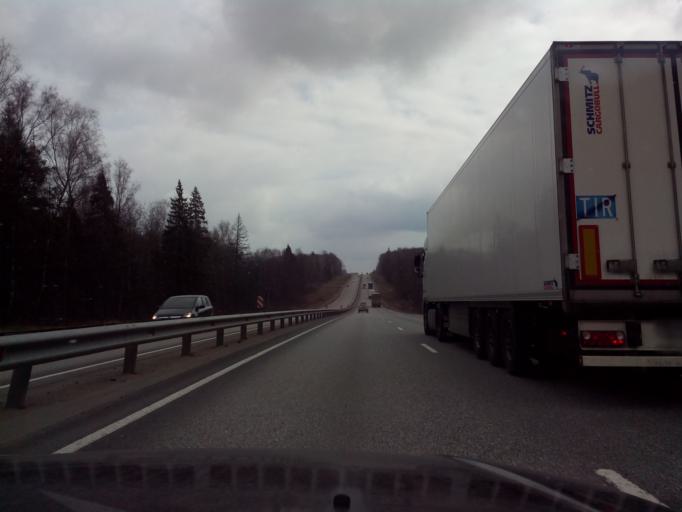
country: RU
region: Vladimir
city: Kosterevo
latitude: 55.9514
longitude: 39.5698
